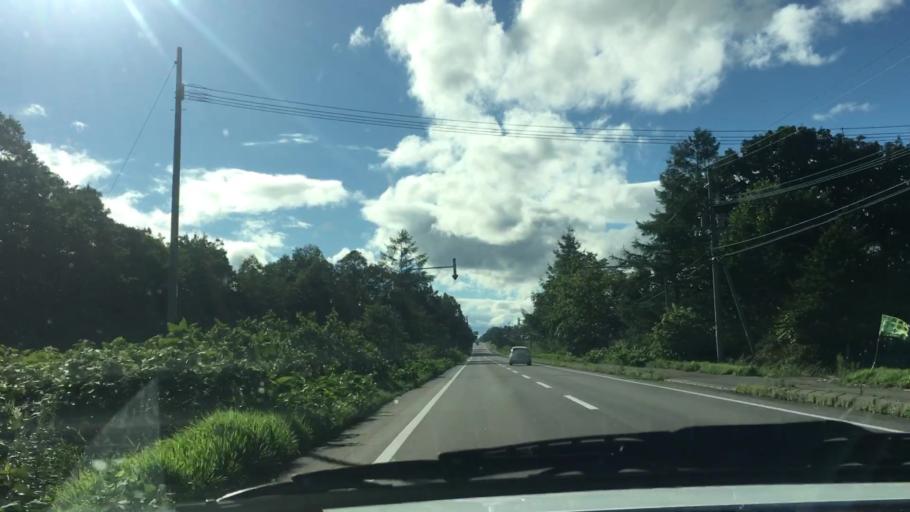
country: JP
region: Hokkaido
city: Otofuke
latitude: 43.1686
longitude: 143.1205
